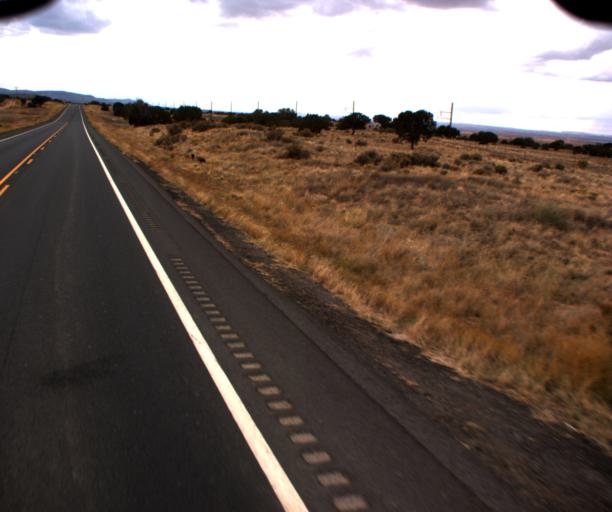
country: US
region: Arizona
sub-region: Navajo County
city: Kayenta
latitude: 36.5008
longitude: -110.6175
